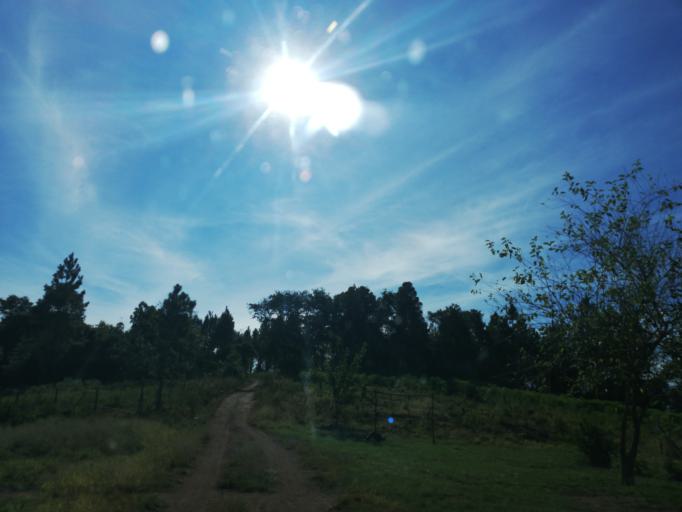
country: AR
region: Misiones
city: Dos de Mayo
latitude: -27.0167
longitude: -54.4226
